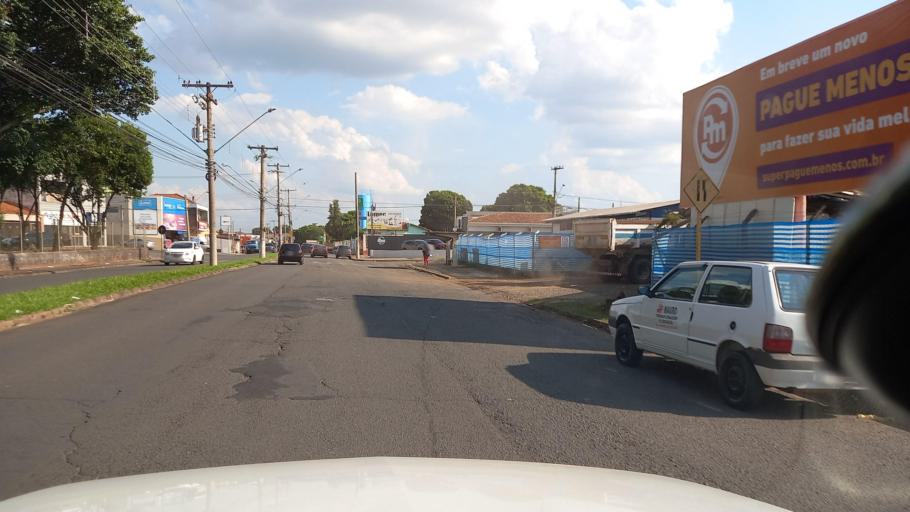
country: BR
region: Sao Paulo
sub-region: Moji-Guacu
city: Mogi-Gaucu
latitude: -22.3520
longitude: -46.9460
